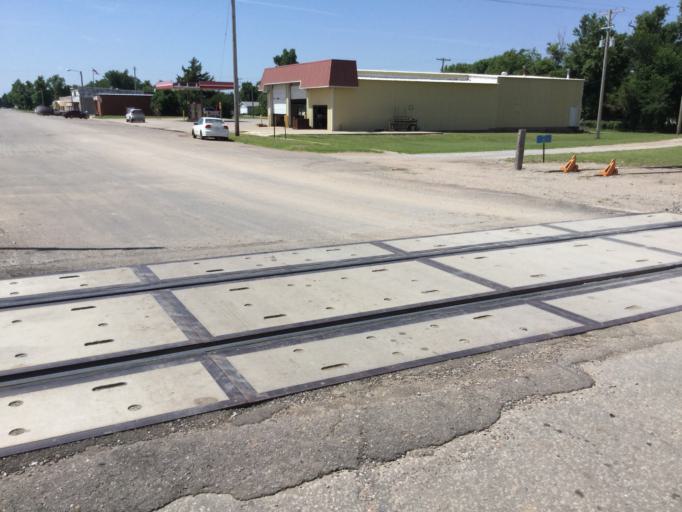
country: US
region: Kansas
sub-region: Edwards County
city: Kinsley
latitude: 37.9398
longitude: -99.2546
